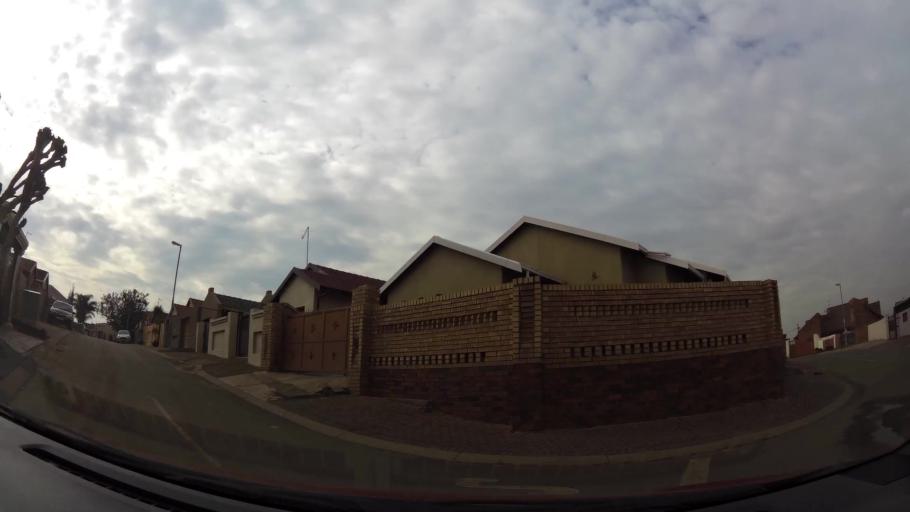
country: ZA
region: Gauteng
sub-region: City of Johannesburg Metropolitan Municipality
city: Soweto
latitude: -26.2727
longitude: 27.8279
